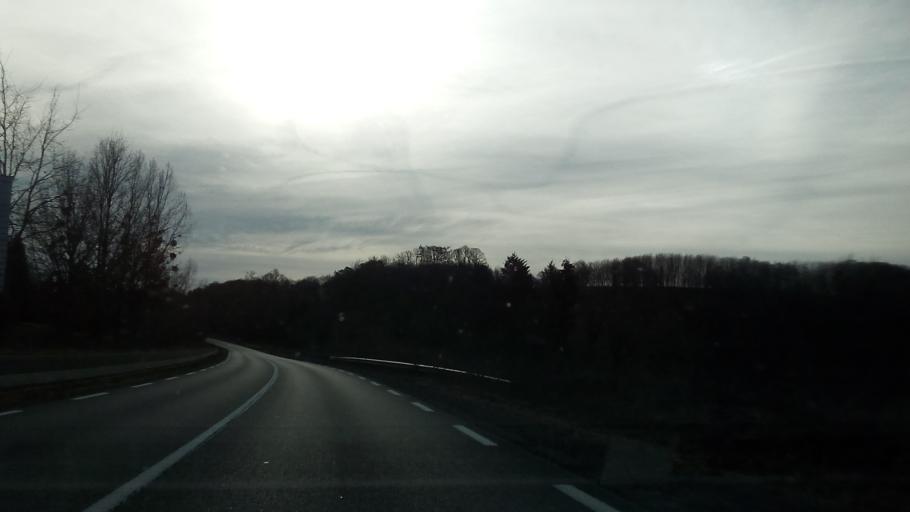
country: FR
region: Limousin
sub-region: Departement de la Correze
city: Seilhac
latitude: 45.3701
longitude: 1.6976
